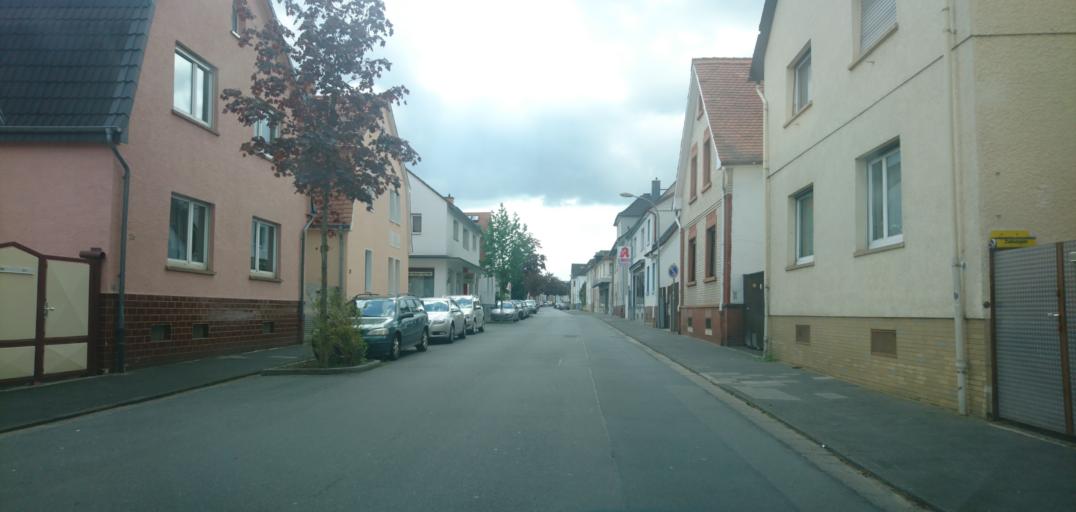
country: DE
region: Hesse
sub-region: Regierungsbezirk Darmstadt
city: Dietzenbach
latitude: 50.0070
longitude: 8.7779
